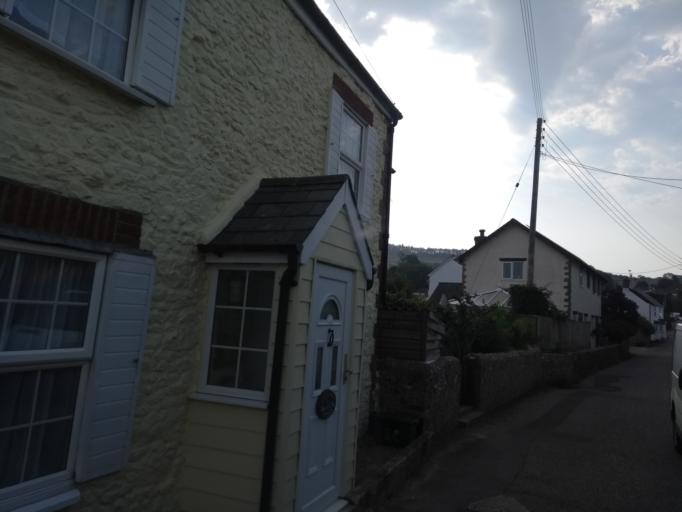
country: GB
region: England
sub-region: Devon
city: Colyton
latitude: 50.7488
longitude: -3.0348
